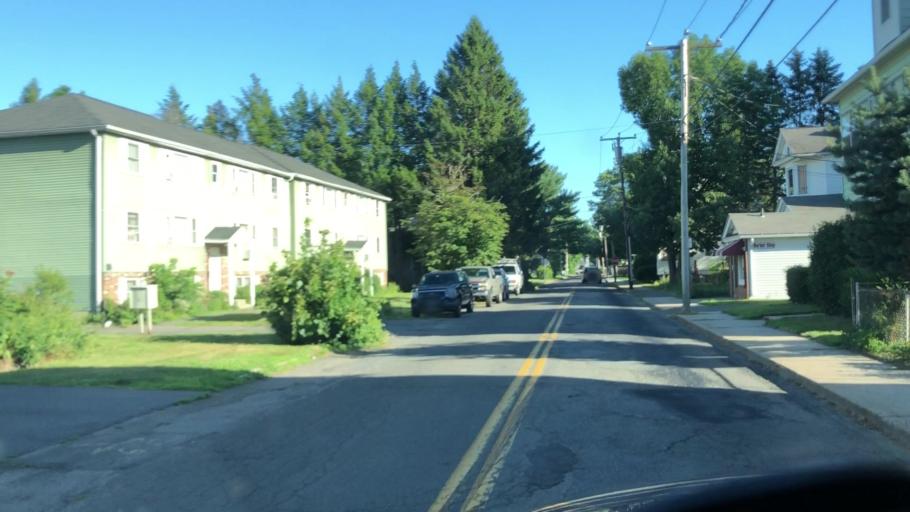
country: US
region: Massachusetts
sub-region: Hampshire County
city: Easthampton
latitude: 42.2676
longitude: -72.6599
